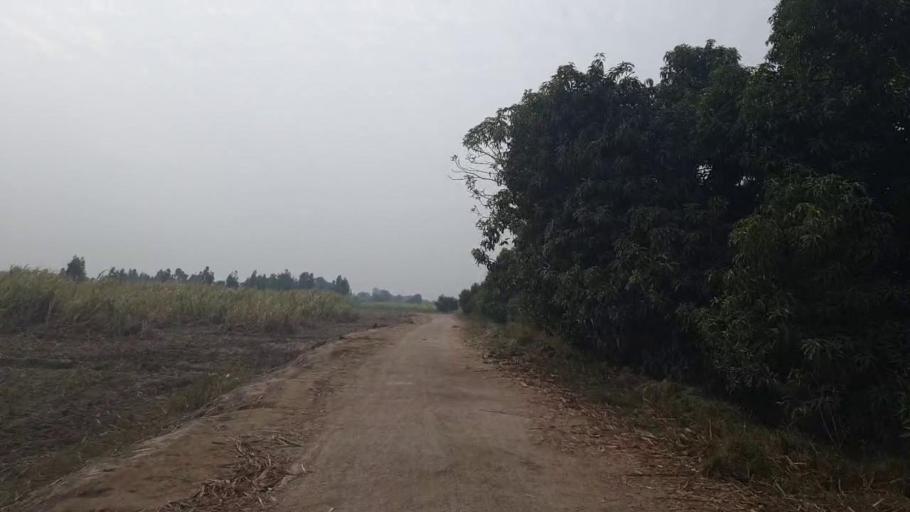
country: PK
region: Sindh
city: Tando Adam
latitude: 25.7166
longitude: 68.7015
